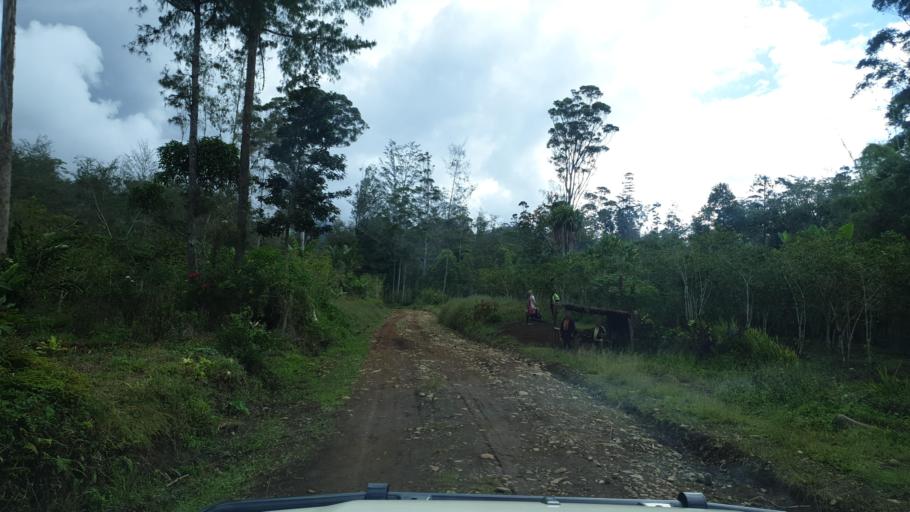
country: PG
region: Eastern Highlands
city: Goroka
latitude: -5.9213
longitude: 145.2637
